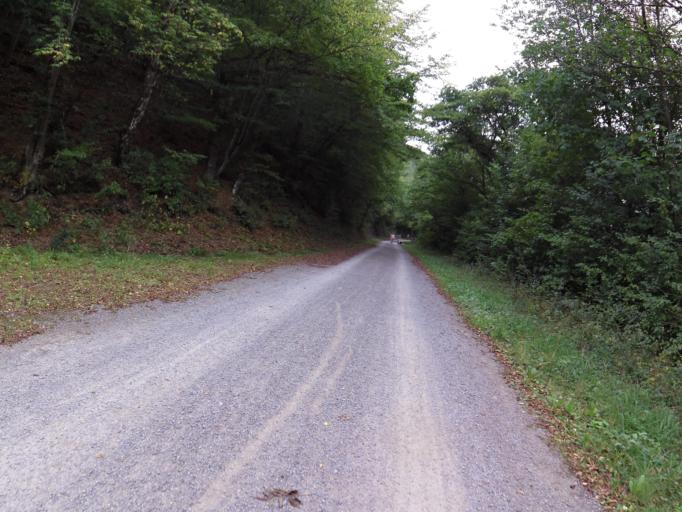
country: DE
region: North Rhine-Westphalia
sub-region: Regierungsbezirk Koln
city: Schleiden
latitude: 50.5814
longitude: 6.4659
